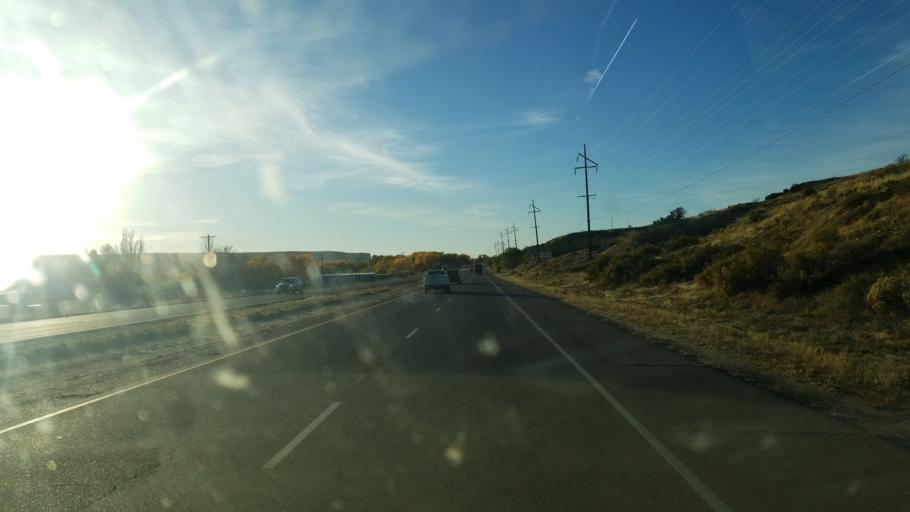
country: US
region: New Mexico
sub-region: San Juan County
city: Lee Acres
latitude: 36.7063
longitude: -108.1183
